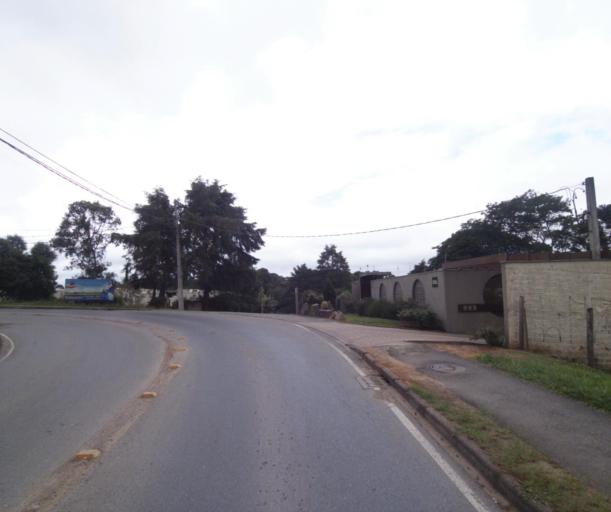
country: BR
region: Parana
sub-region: Quatro Barras
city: Quatro Barras
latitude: -25.3602
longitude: -49.1084
